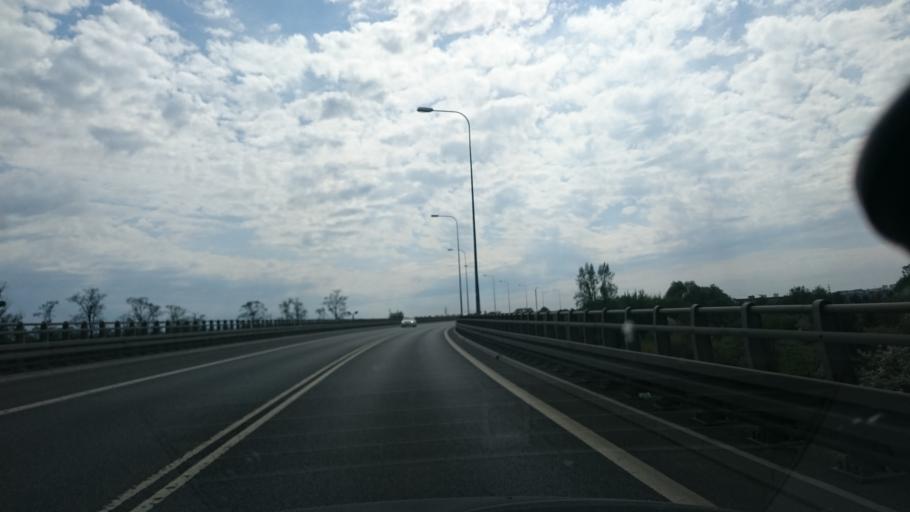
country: PL
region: Kujawsko-Pomorskie
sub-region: Grudziadz
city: Grudziadz
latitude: 53.4826
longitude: 18.7908
